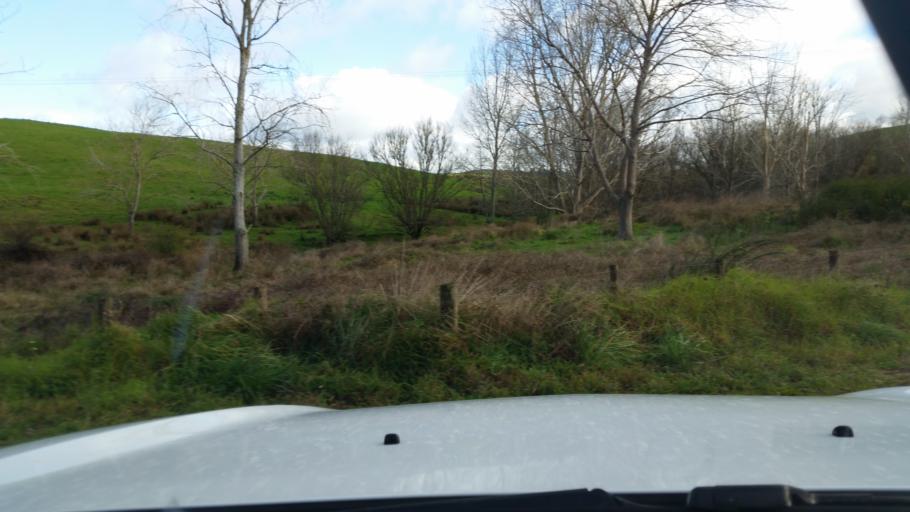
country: NZ
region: Northland
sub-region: Whangarei
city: Maungatapere
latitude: -35.6932
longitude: 174.1050
